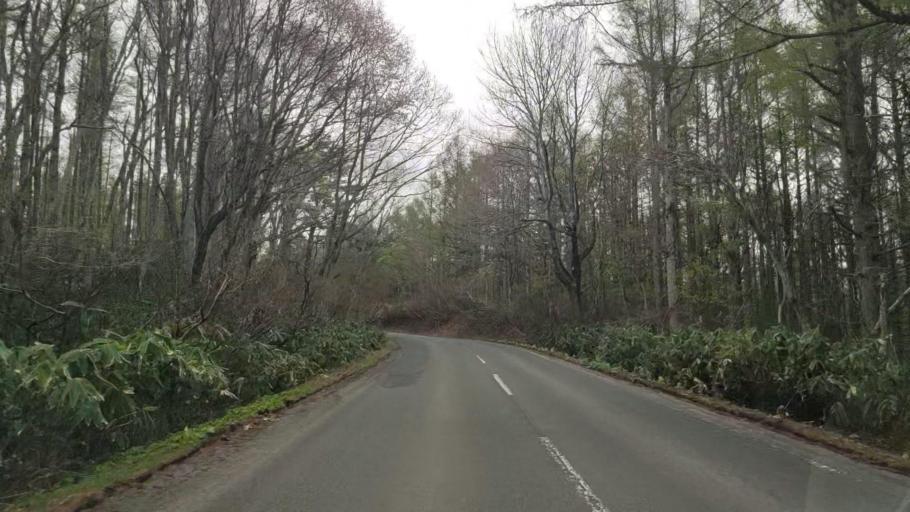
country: JP
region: Aomori
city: Aomori Shi
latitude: 40.7248
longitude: 140.8498
